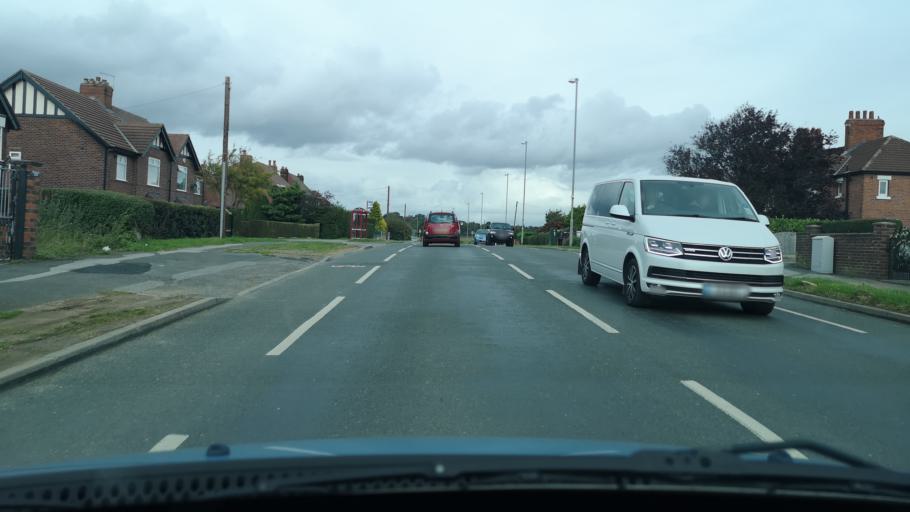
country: GB
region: England
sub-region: City and Borough of Wakefield
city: Featherstone
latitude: 53.6767
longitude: -1.3411
